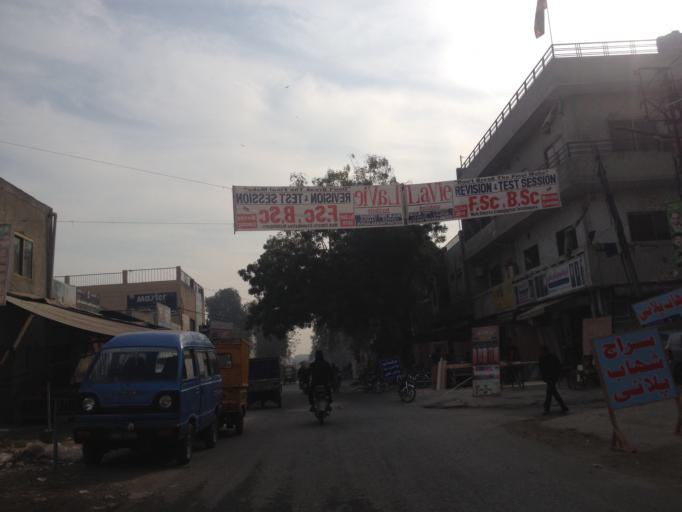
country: PK
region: Punjab
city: Lahore
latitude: 31.4655
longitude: 74.3081
